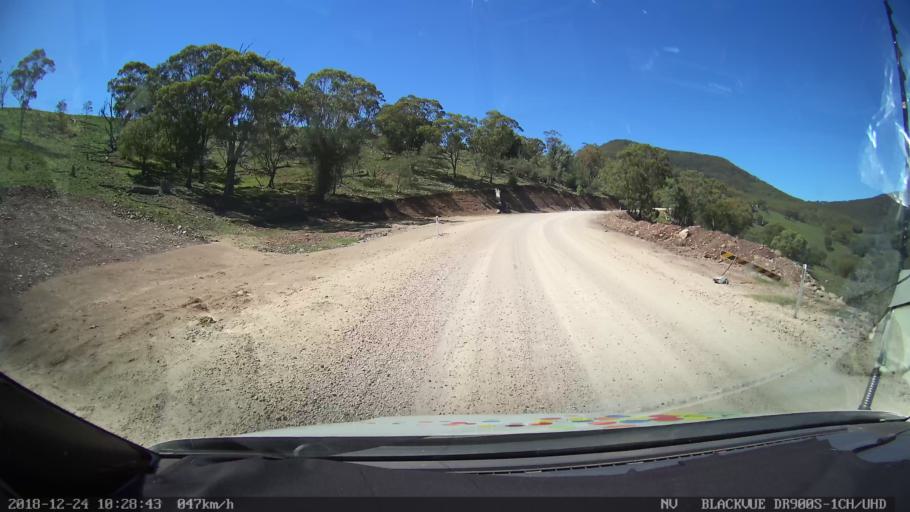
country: AU
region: New South Wales
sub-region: Liverpool Plains
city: Quirindi
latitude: -31.8279
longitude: 150.5316
